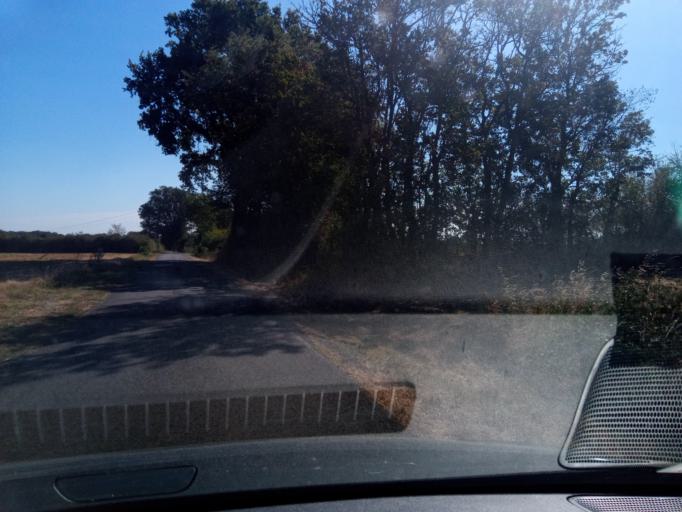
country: FR
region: Poitou-Charentes
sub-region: Departement de la Vienne
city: Lussac-les-Chateaux
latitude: 46.3989
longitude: 0.7446
